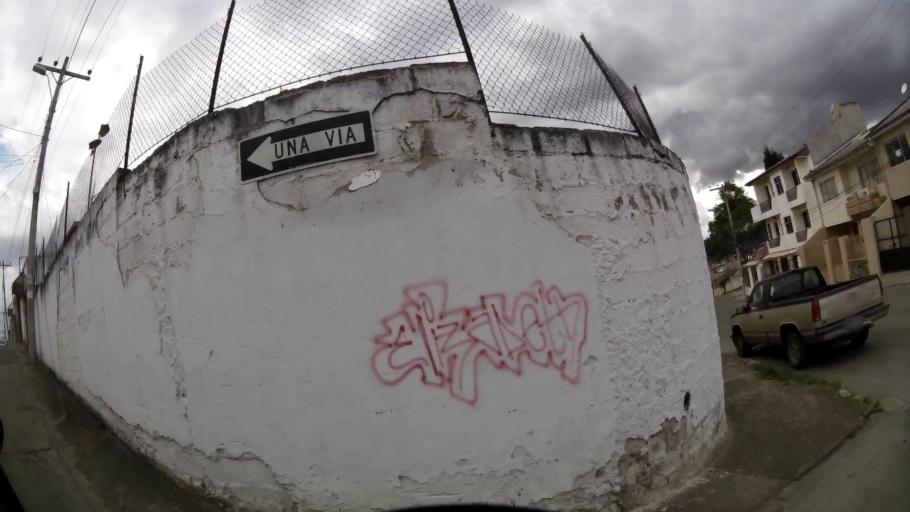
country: EC
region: Azuay
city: Cuenca
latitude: -2.8859
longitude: -79.0047
